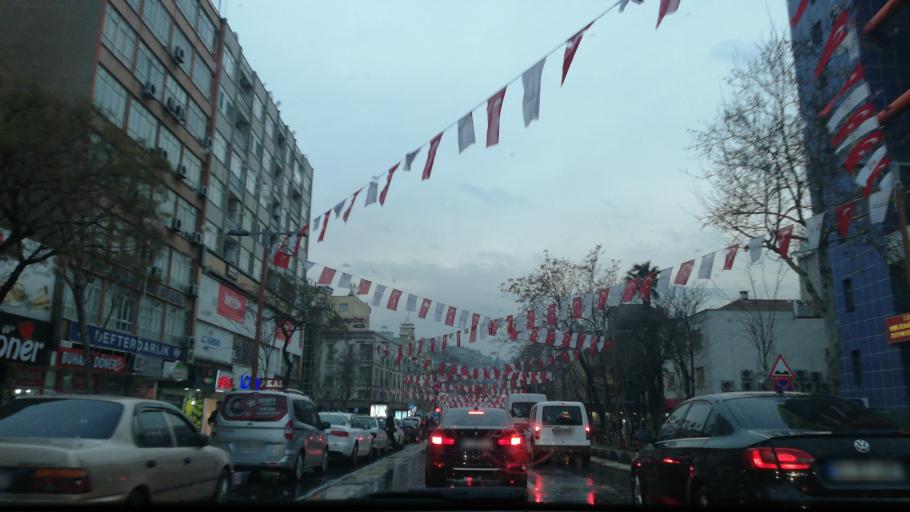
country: TR
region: Kahramanmaras
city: Kahramanmaras
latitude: 37.5800
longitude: 36.9288
